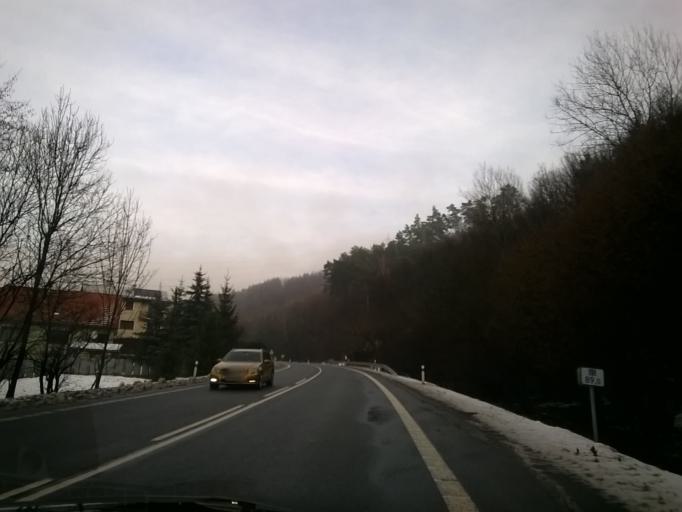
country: SK
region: Banskobystricky
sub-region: Okres Ziar nad Hronom
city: Kremnica
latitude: 48.6801
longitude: 18.9176
